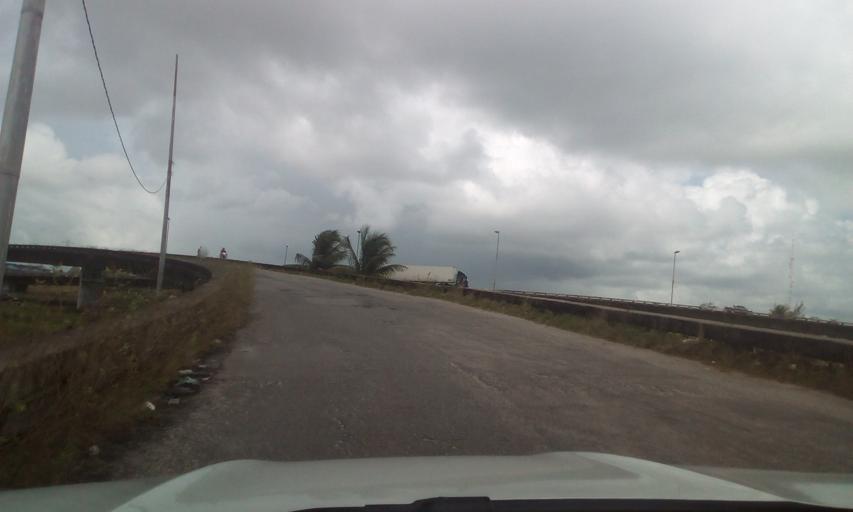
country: BR
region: Pernambuco
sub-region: Recife
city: Recife
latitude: -8.0644
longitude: -34.9425
